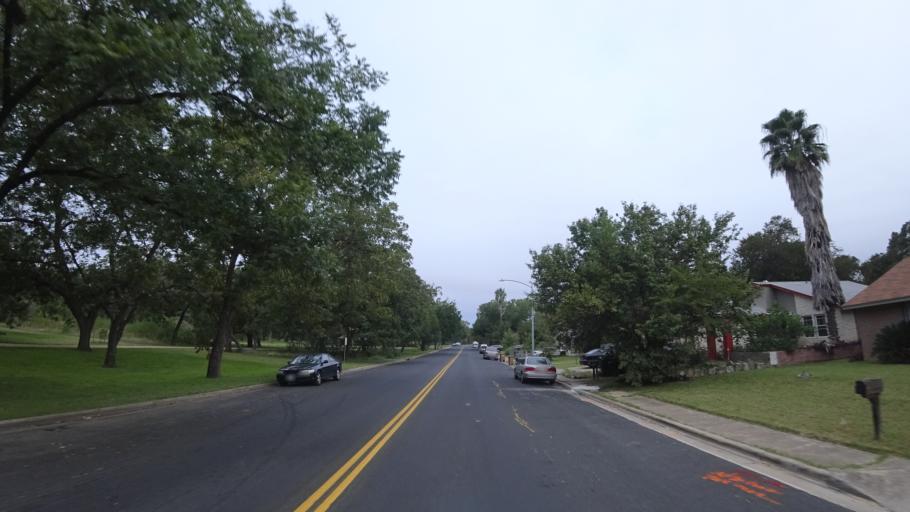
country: US
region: Texas
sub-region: Travis County
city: Austin
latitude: 30.2666
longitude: -97.7121
